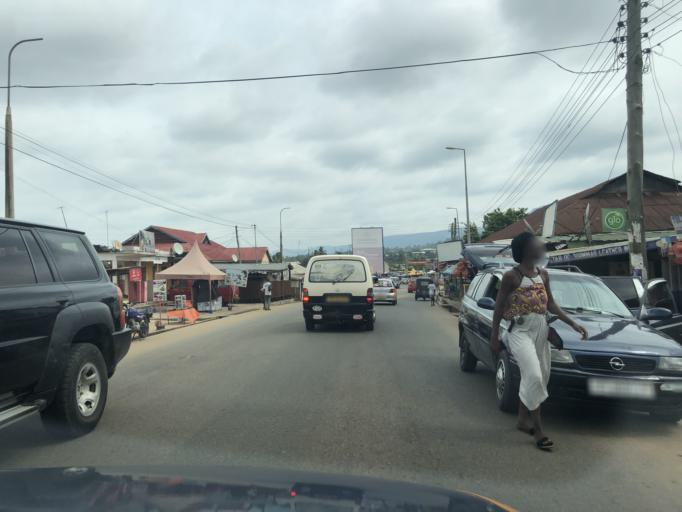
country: GH
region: Eastern
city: Koforidua
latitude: 6.1105
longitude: -0.2689
